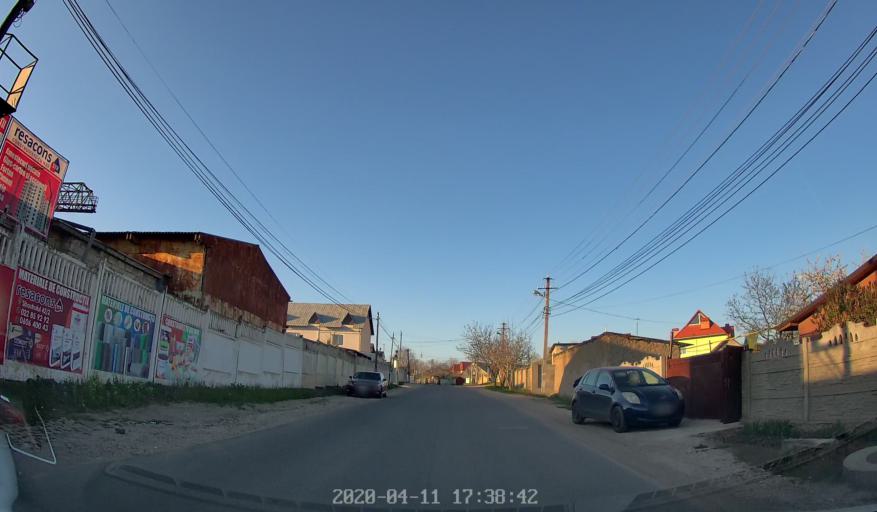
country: MD
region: Laloveni
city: Ialoveni
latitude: 46.9838
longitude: 28.8038
